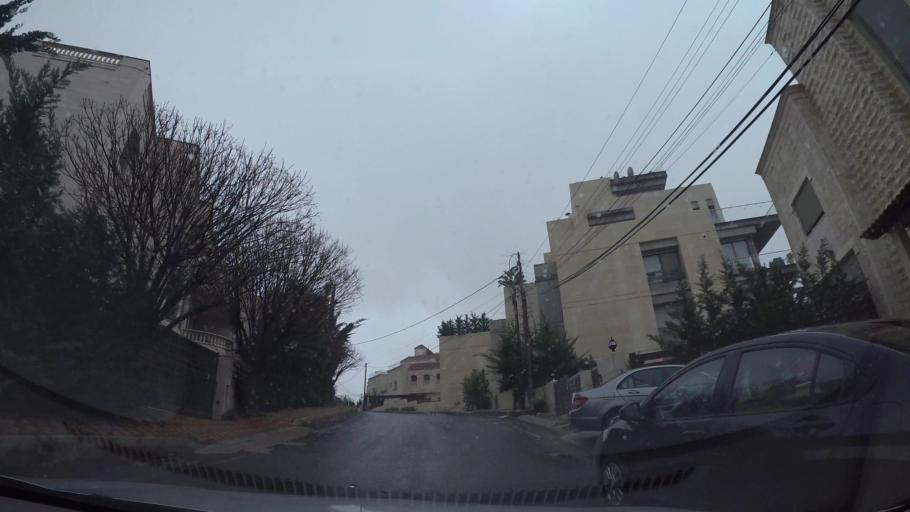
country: JO
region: Amman
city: Wadi as Sir
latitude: 31.9990
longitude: 35.8177
